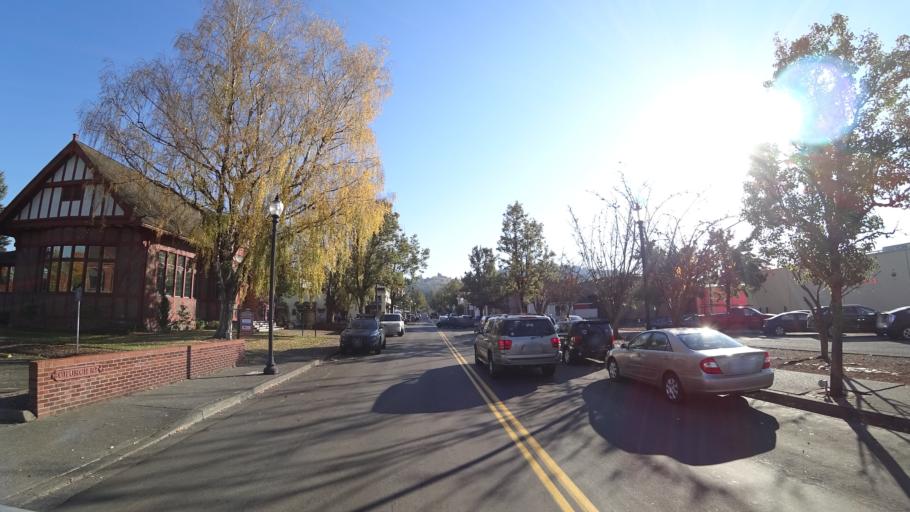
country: US
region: Oregon
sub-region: Multnomah County
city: Gresham
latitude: 45.5008
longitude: -122.4309
